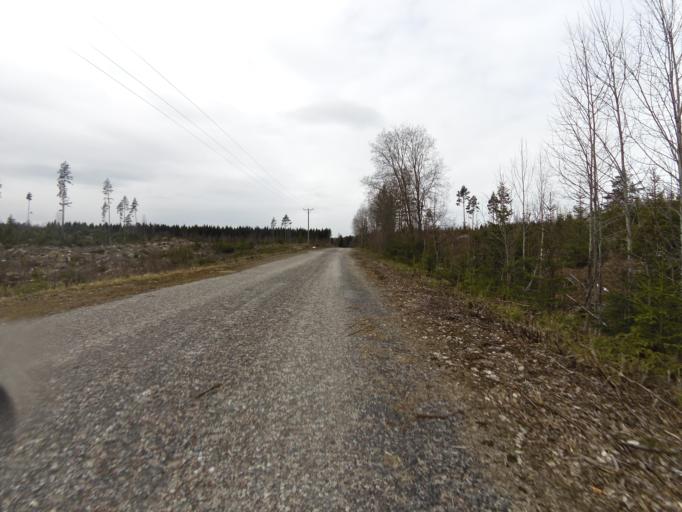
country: SE
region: Gaevleborg
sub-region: Hofors Kommun
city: Hofors
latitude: 60.5402
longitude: 16.2067
